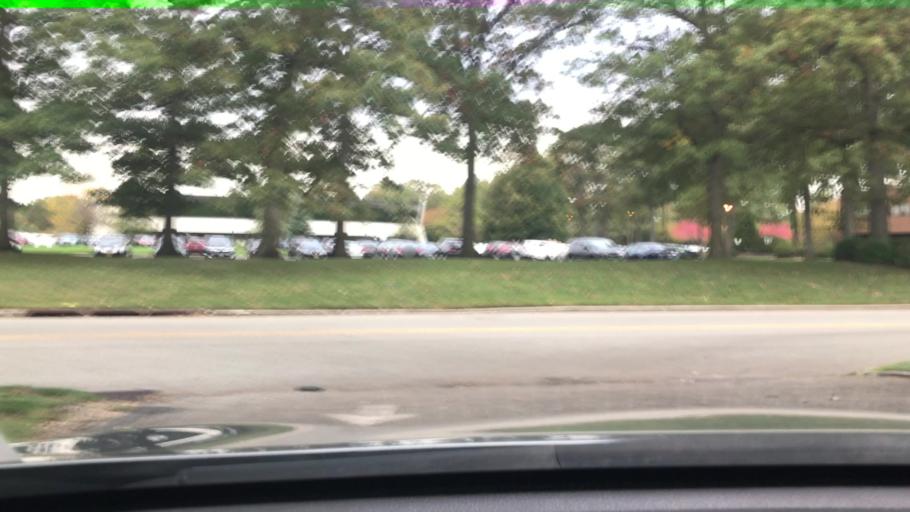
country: US
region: New York
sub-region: Nassau County
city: Syosset
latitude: 40.8061
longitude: -73.4873
